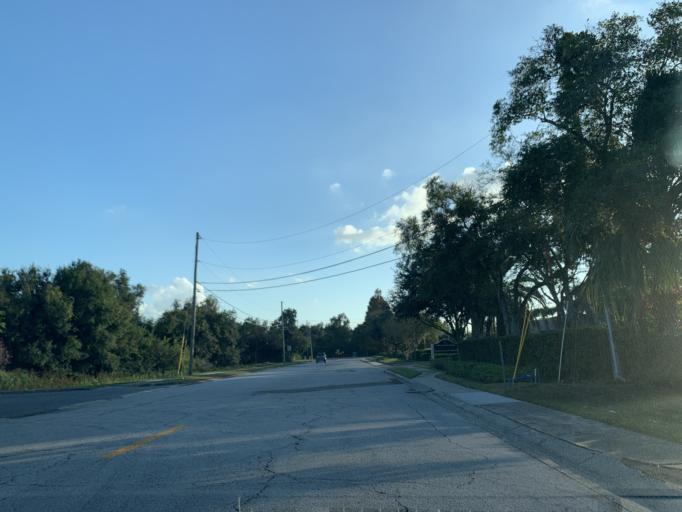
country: US
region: Florida
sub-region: Pinellas County
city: South Highpoint
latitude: 27.9584
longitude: -82.7329
